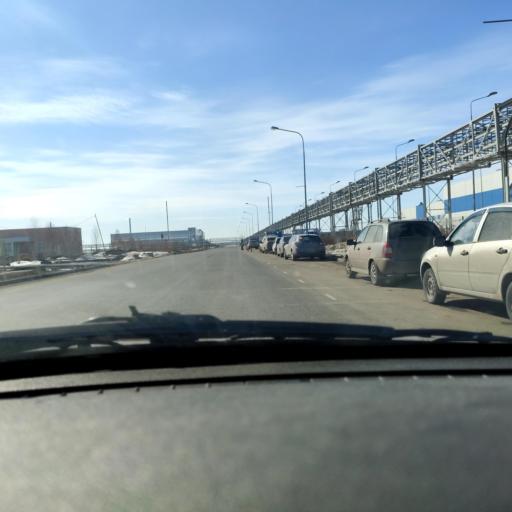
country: RU
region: Samara
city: Podstepki
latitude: 53.5602
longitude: 49.1846
